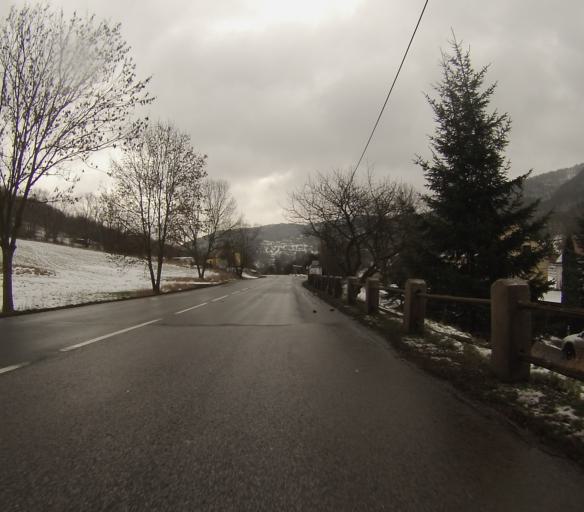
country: CZ
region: Ustecky
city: Benesov nad Ploucnici
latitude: 50.7515
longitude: 14.2604
